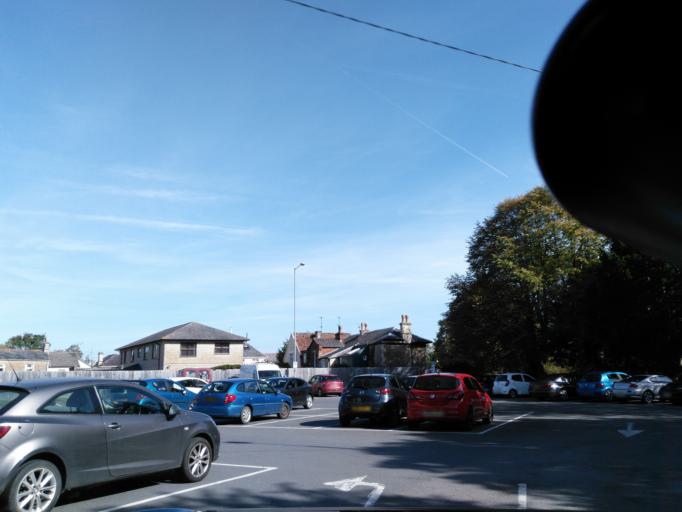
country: GB
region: England
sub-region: Wiltshire
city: Melksham
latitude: 51.3741
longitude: -2.1360
